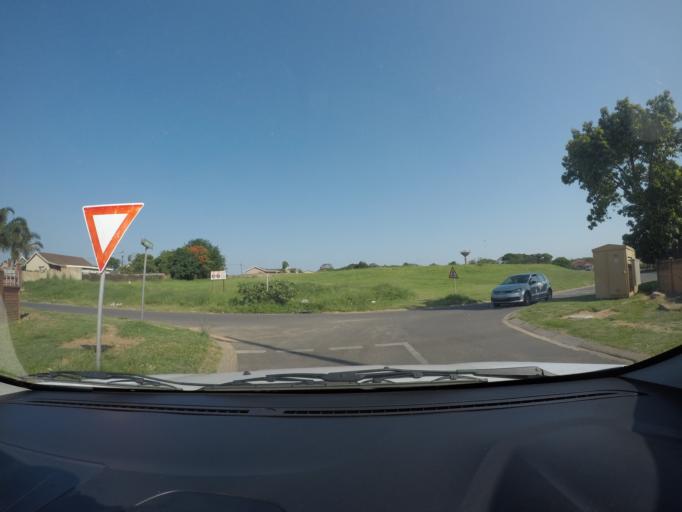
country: ZA
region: KwaZulu-Natal
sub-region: uThungulu District Municipality
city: Richards Bay
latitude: -28.7189
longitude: 32.0397
